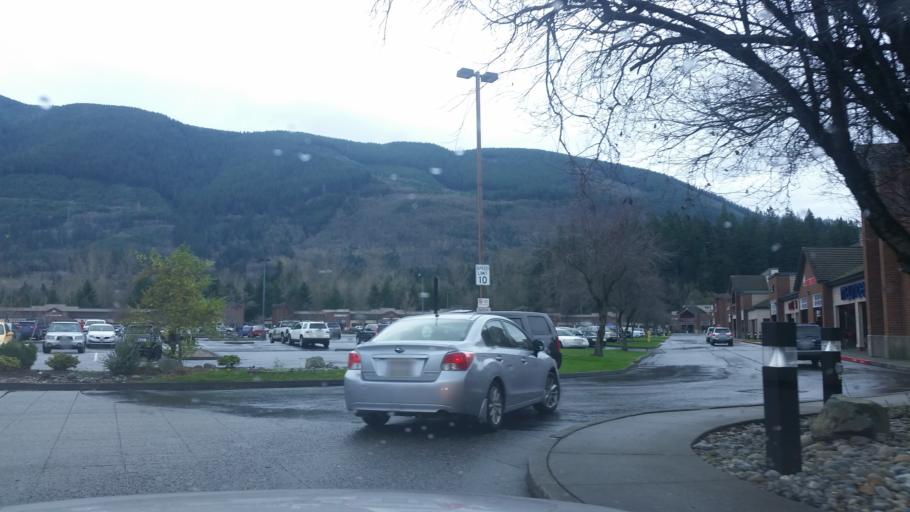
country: US
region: Washington
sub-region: King County
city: North Bend
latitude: 47.4917
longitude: -121.7934
